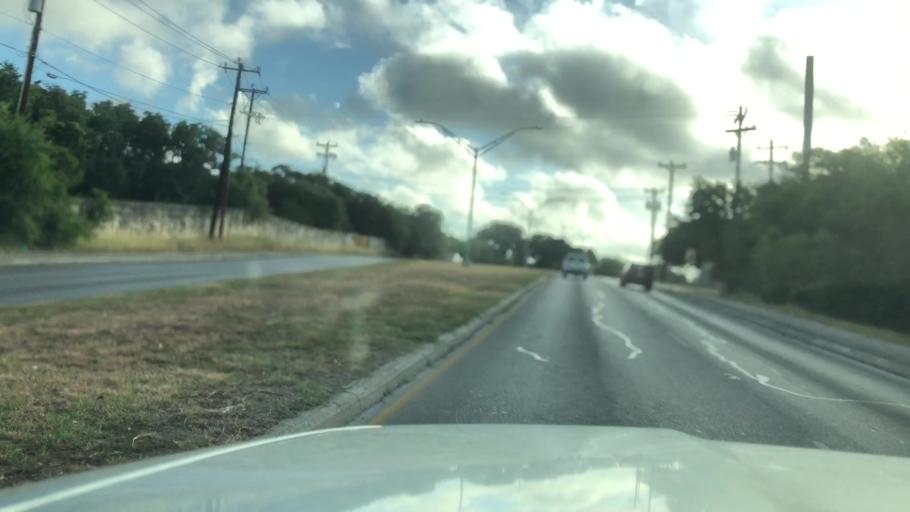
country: US
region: Texas
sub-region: Bexar County
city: Shavano Park
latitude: 29.5711
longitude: -98.5509
